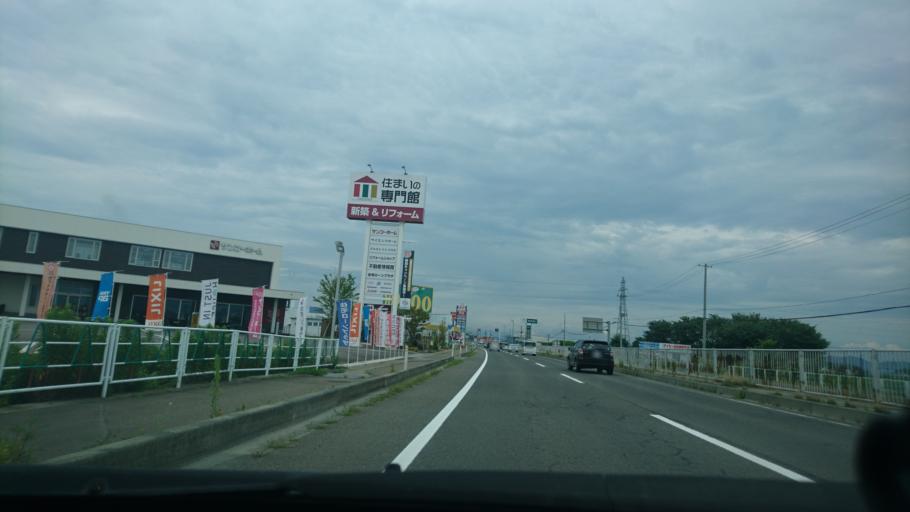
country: JP
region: Akita
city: Omagari
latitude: 39.4525
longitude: 140.4995
